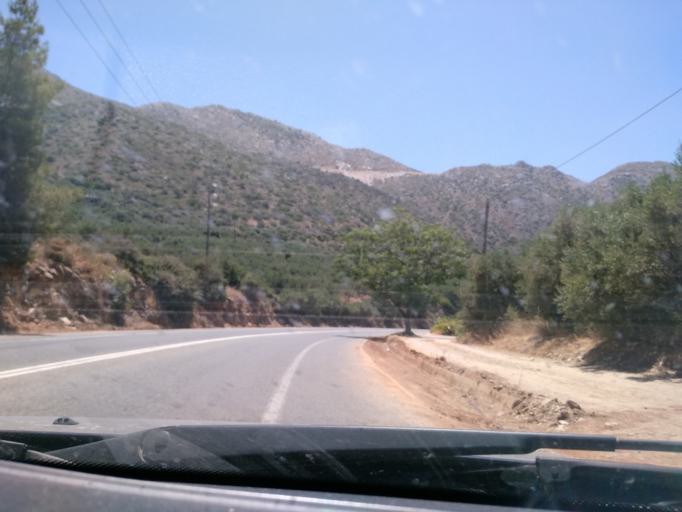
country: GR
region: Crete
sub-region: Nomos Rethymnis
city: Anogeia
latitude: 35.3877
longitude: 24.8868
